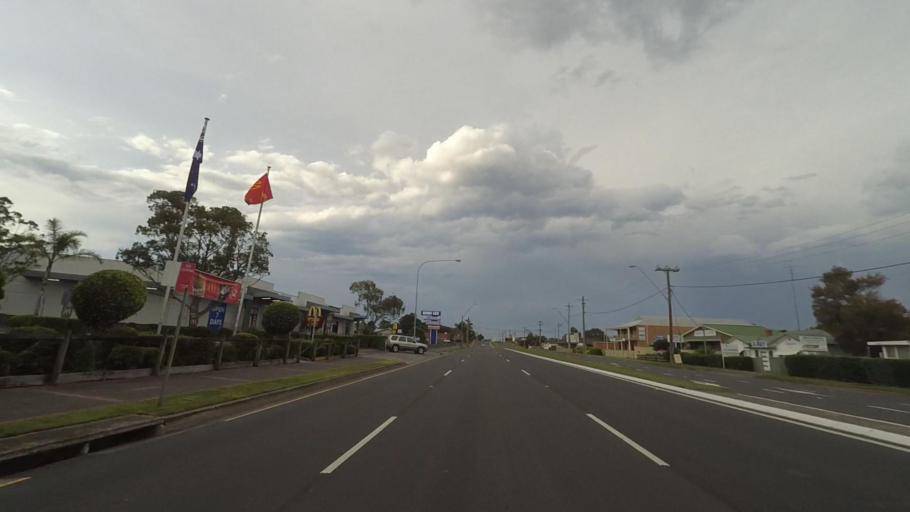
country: AU
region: New South Wales
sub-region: Shellharbour
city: Lake Illawarra
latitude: -34.5522
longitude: 150.8600
